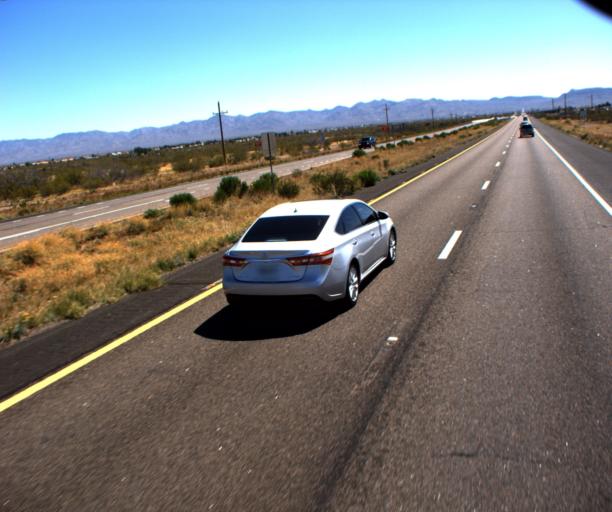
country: US
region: Arizona
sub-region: Mohave County
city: Golden Valley
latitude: 35.2254
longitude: -114.2878
